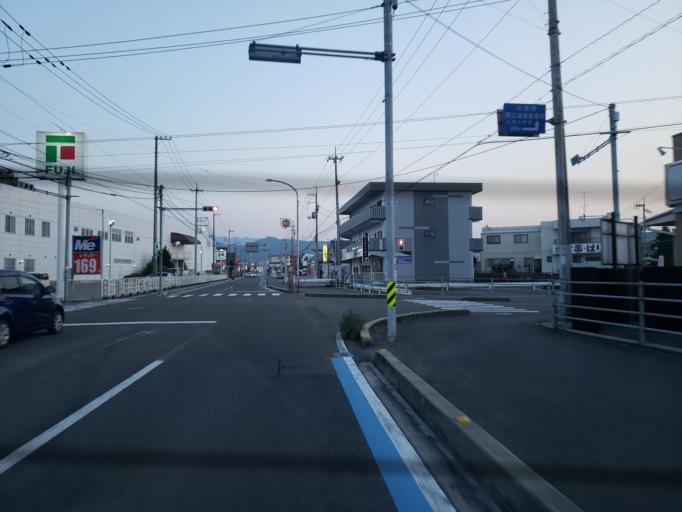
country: JP
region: Ehime
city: Hojo
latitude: 34.0484
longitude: 132.9809
